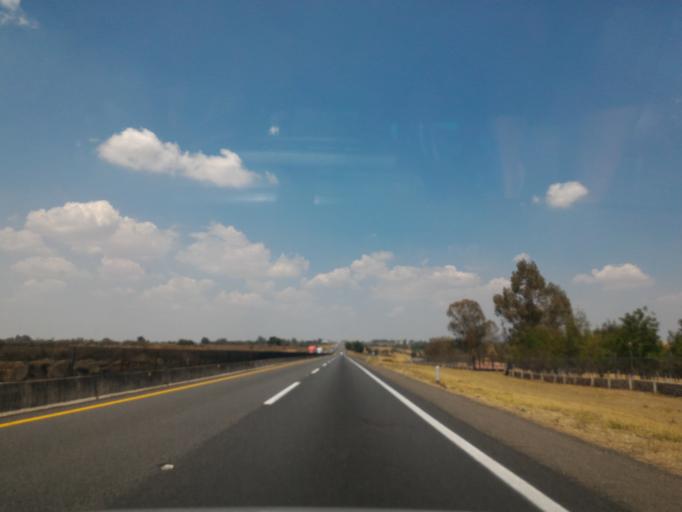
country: MX
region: Jalisco
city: Tepatitlan de Morelos
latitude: 20.8753
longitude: -102.7424
